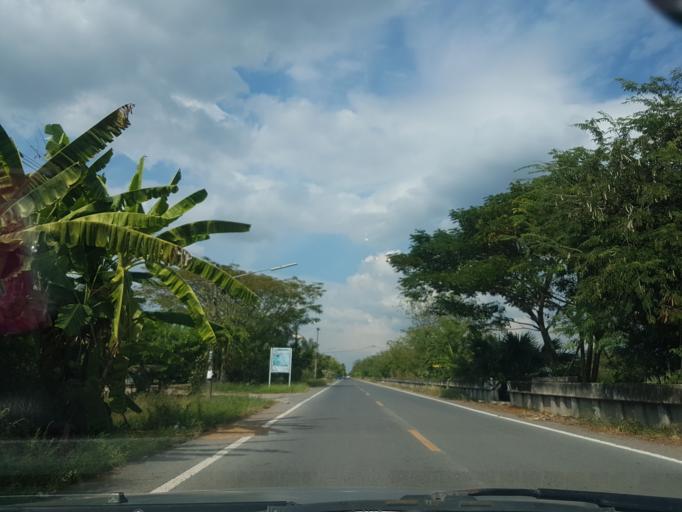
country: TH
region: Pathum Thani
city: Nong Suea
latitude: 14.1663
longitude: 100.8915
